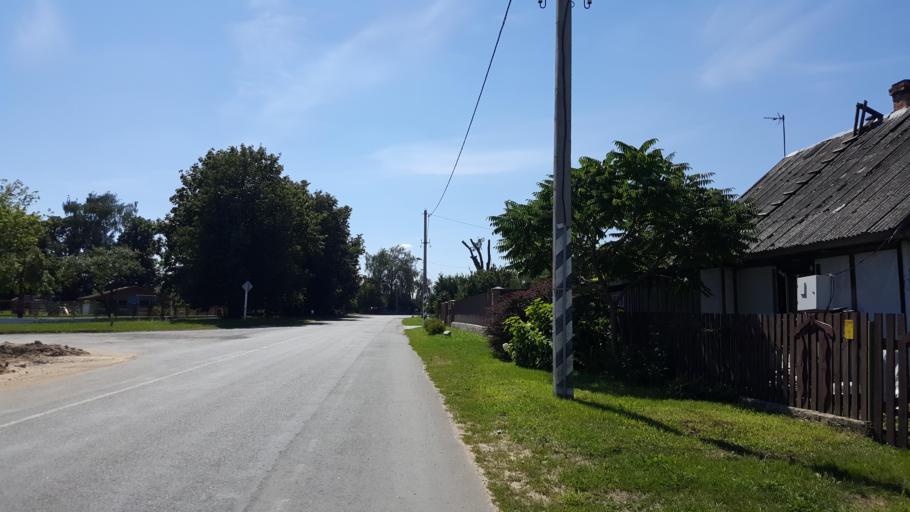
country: BY
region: Brest
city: Charnawchytsy
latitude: 52.2687
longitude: 23.5864
